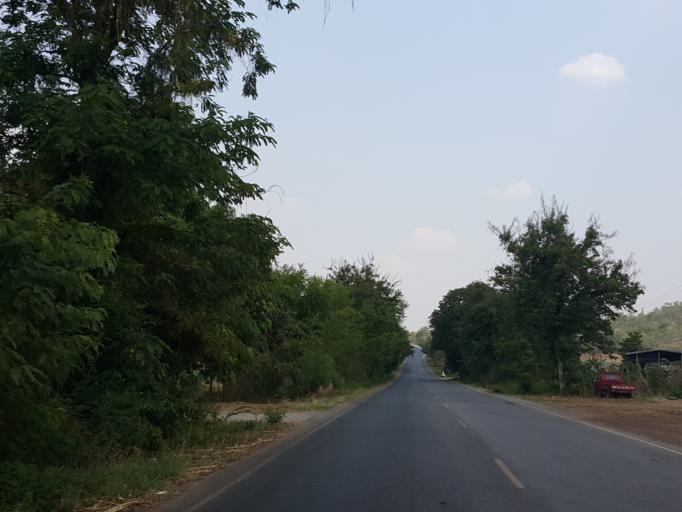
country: TH
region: Kanchanaburi
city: Nong Prue
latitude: 14.5360
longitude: 99.5829
